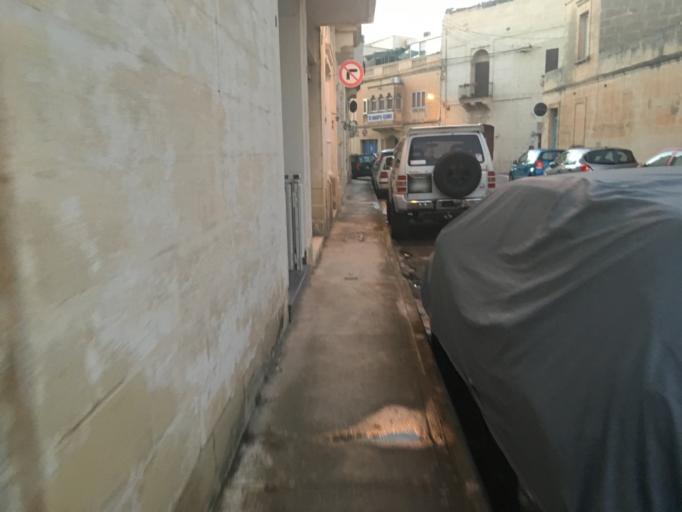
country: MT
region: Il-Mosta
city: Mosta
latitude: 35.9088
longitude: 14.4294
